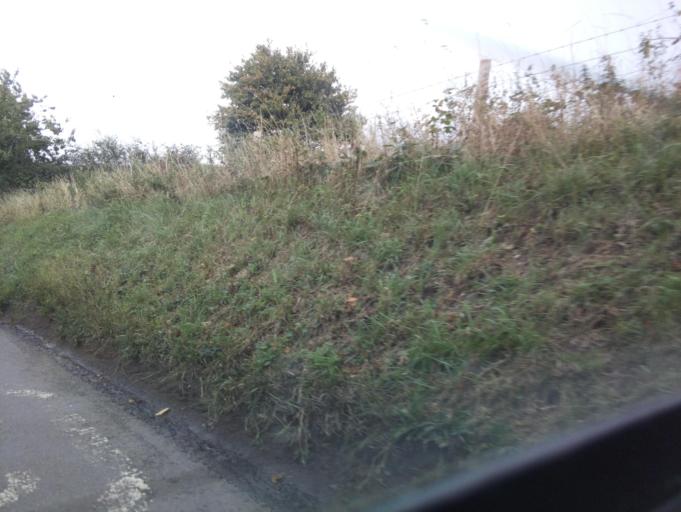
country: GB
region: England
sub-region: Shropshire
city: Woodcote
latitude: 52.7072
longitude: -2.3559
